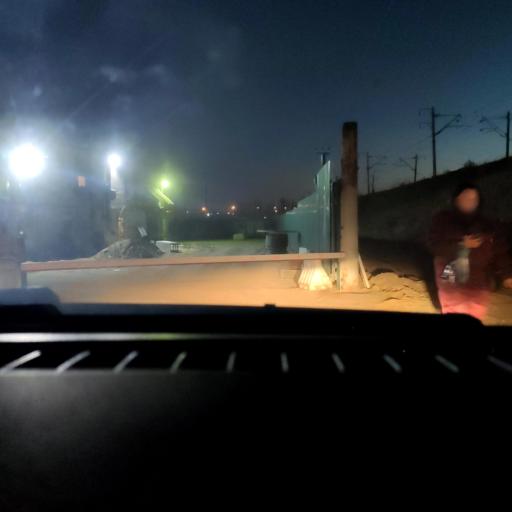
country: RU
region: Voronezj
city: Maslovka
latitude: 51.6245
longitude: 39.2577
